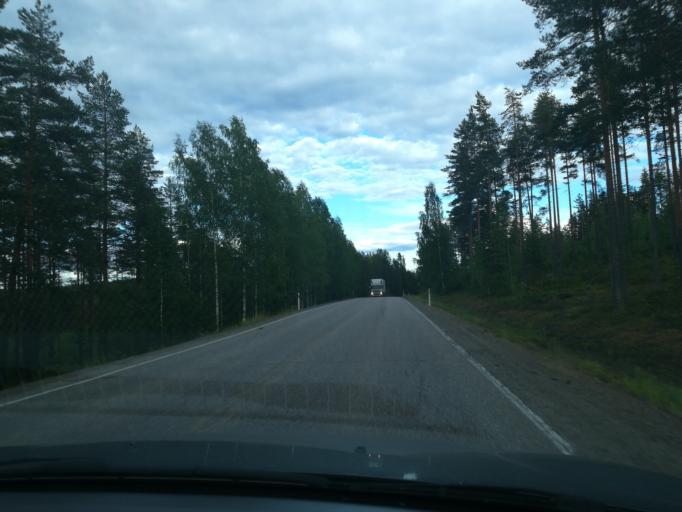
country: FI
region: South Karelia
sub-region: Lappeenranta
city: Savitaipale
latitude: 61.5120
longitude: 27.7816
